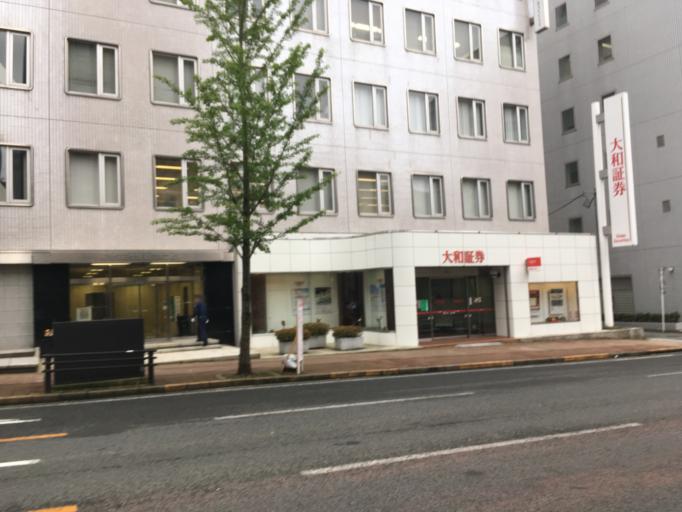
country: JP
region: Akita
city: Akita
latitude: 39.7160
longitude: 140.1248
